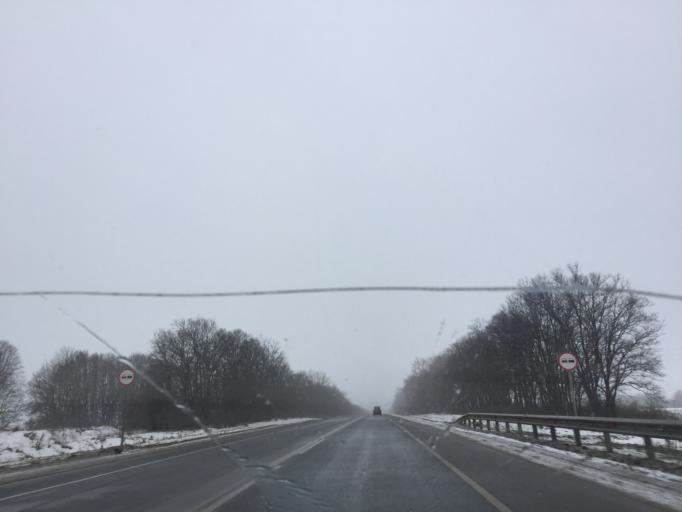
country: RU
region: Tula
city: Plavsk
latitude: 53.8064
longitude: 37.3857
